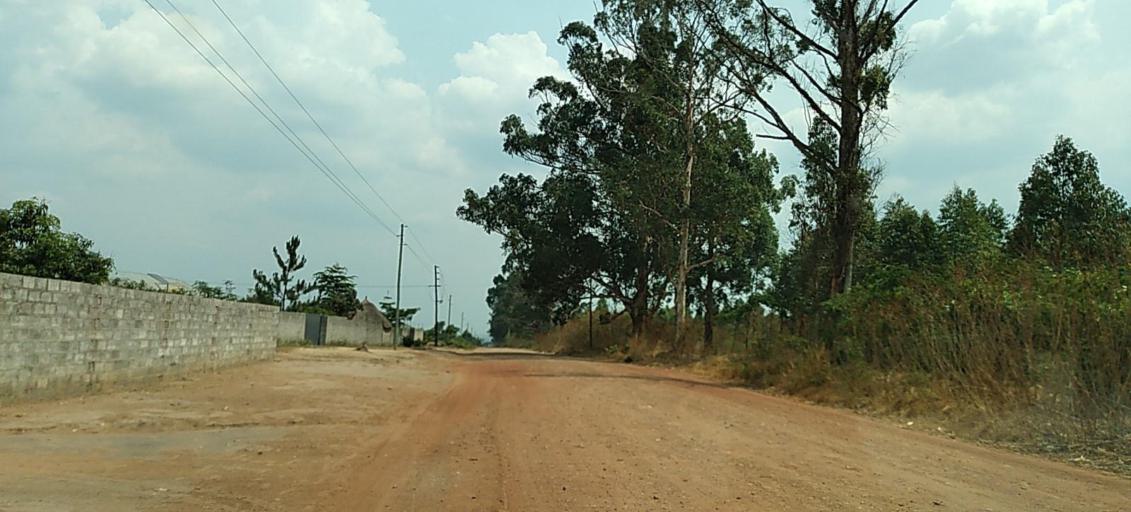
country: ZM
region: Copperbelt
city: Kalulushi
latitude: -12.8440
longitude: 28.0779
